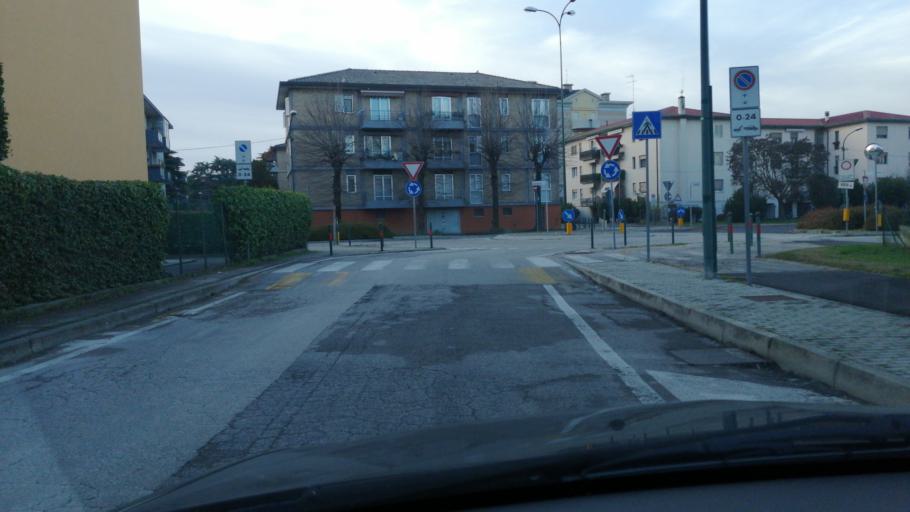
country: IT
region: Veneto
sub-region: Provincia di Venezia
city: Zelarino
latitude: 45.4865
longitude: 12.2108
